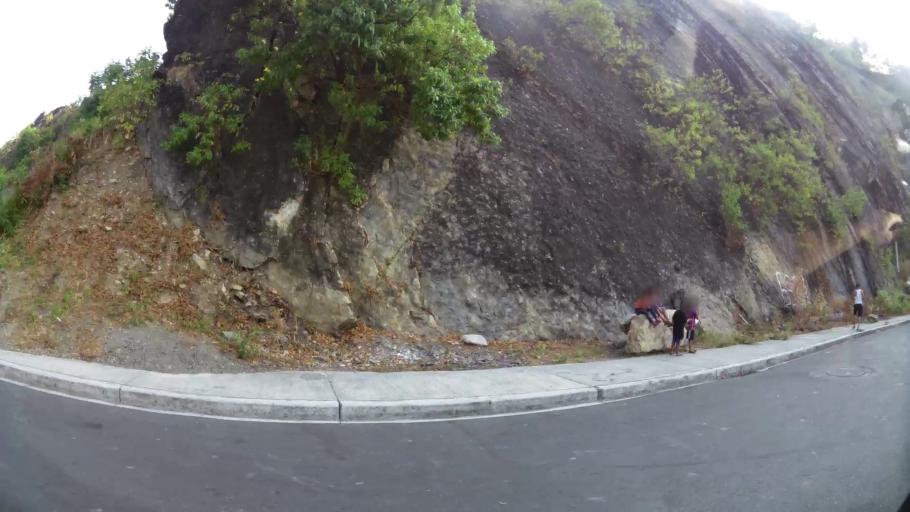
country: EC
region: Guayas
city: Guayaquil
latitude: -2.1864
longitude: -79.9084
